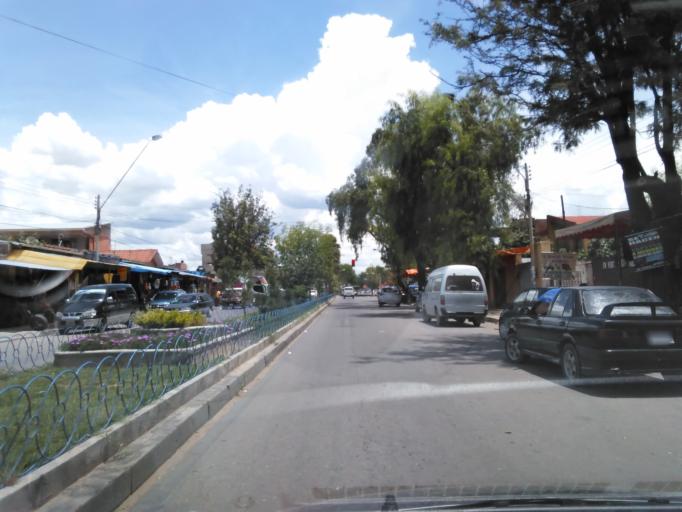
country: BO
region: Cochabamba
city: Cochabamba
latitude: -17.4086
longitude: -66.1642
